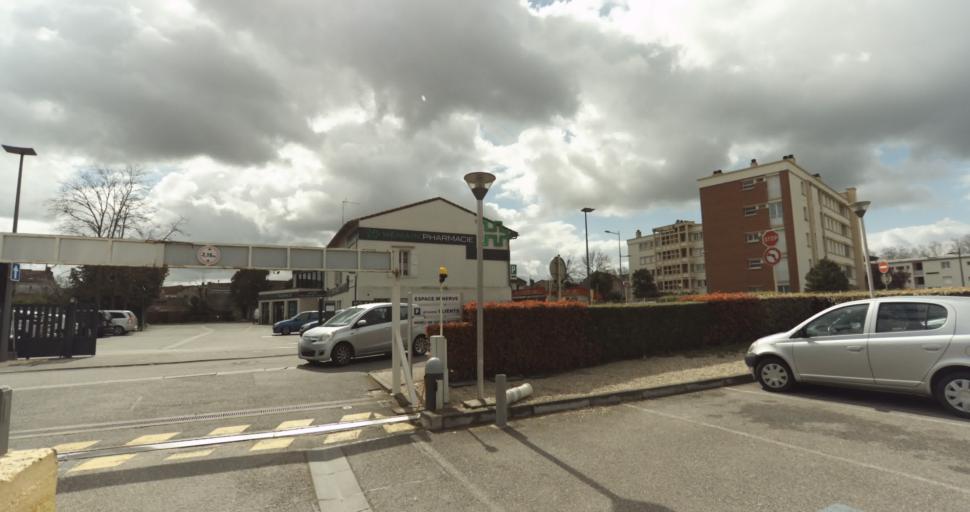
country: FR
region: Midi-Pyrenees
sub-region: Departement de la Haute-Garonne
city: Auterive
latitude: 43.3508
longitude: 1.4708
